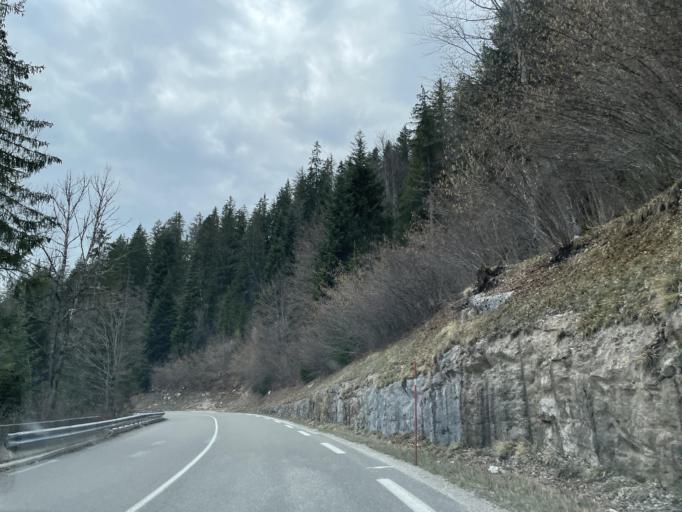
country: FR
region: Franche-Comte
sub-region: Departement du Doubs
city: Gilley
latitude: 47.0164
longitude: 6.4874
